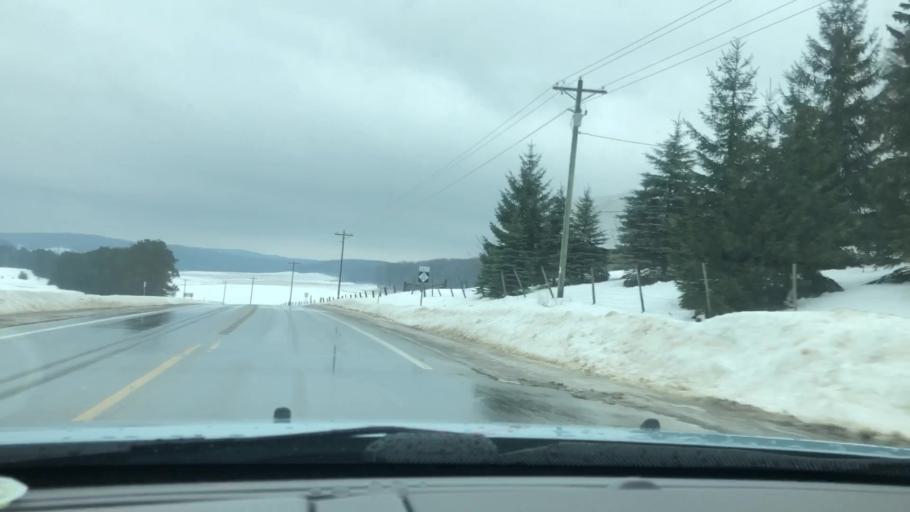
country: US
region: Michigan
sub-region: Charlevoix County
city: Boyne City
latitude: 45.0952
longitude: -84.9787
